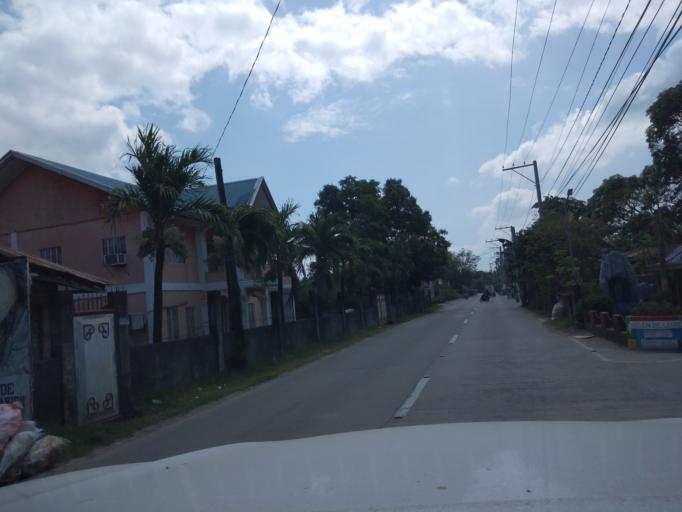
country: PH
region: Central Luzon
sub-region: Province of Pampanga
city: Lourdes
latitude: 15.0201
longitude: 120.8493
